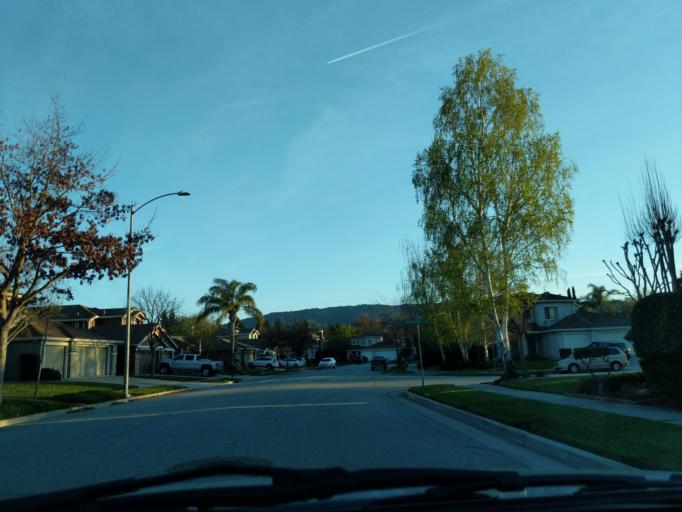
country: US
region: California
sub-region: Santa Clara County
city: Gilroy
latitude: 37.0300
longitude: -121.6036
